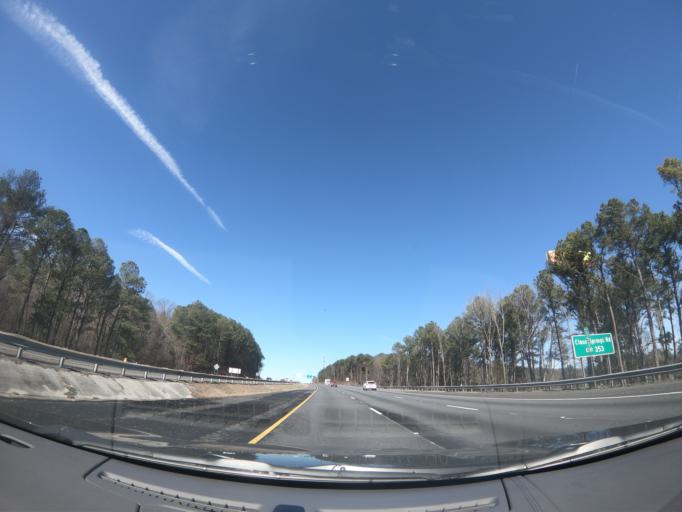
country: US
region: Georgia
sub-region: Catoosa County
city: Indian Springs
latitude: 34.9629
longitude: -85.1848
